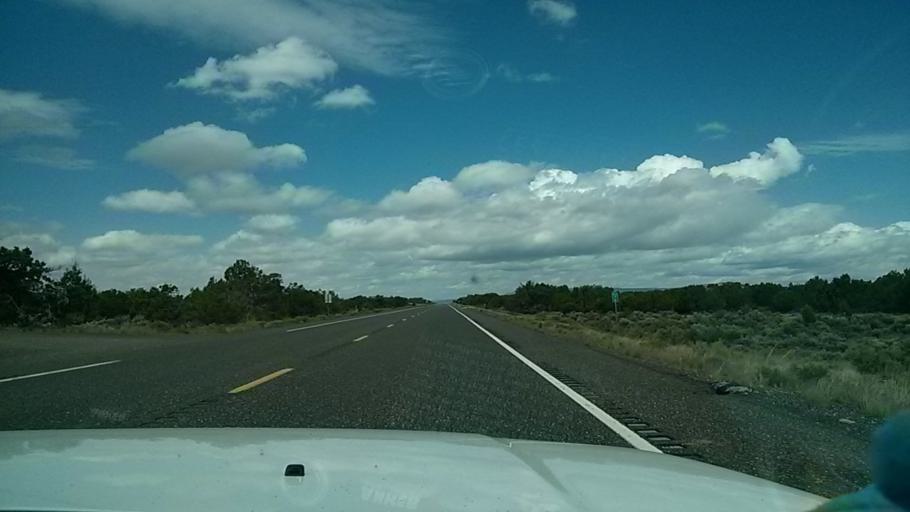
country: US
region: Utah
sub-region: Kane County
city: Kanab
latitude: 37.1763
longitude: -112.6265
